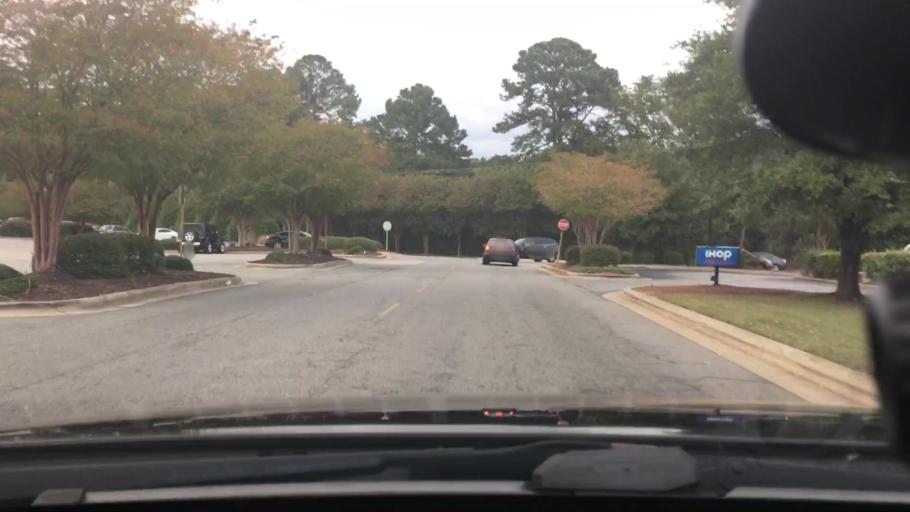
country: US
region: North Carolina
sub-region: Pitt County
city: Summerfield
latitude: 35.5804
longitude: -77.3819
